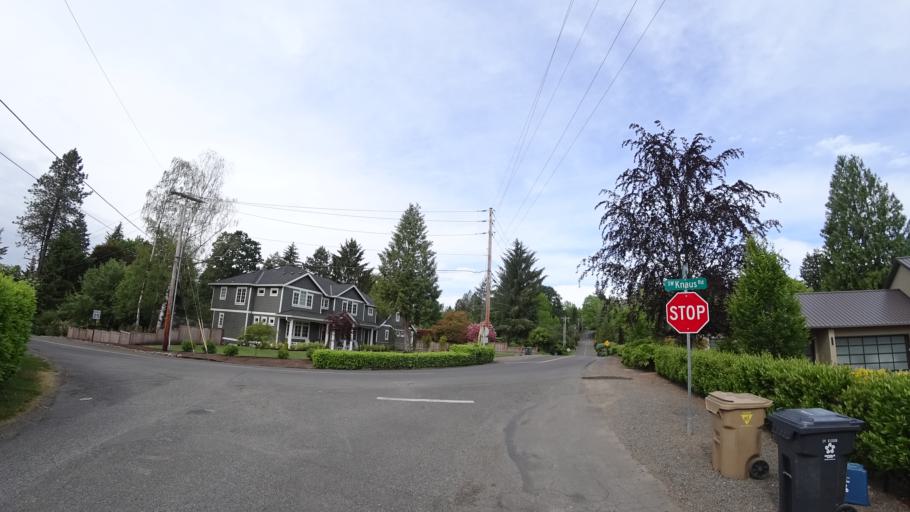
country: US
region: Oregon
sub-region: Clackamas County
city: Lake Oswego
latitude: 45.4257
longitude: -122.6888
